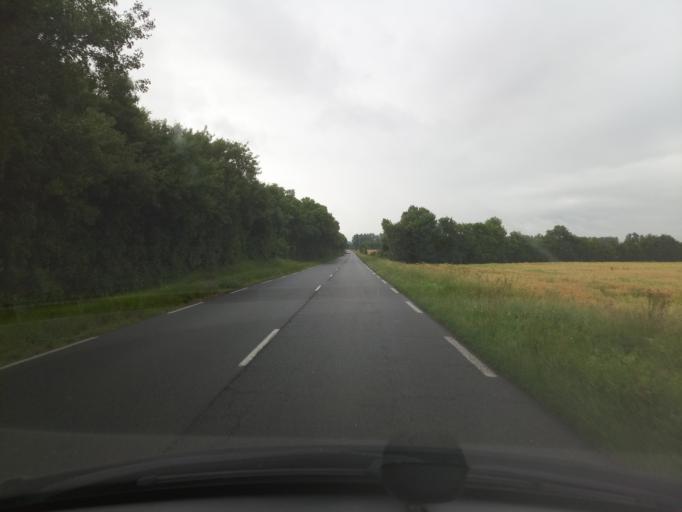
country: FR
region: Poitou-Charentes
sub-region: Departement de la Charente-Maritime
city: Courcon
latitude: 46.1729
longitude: -0.8415
